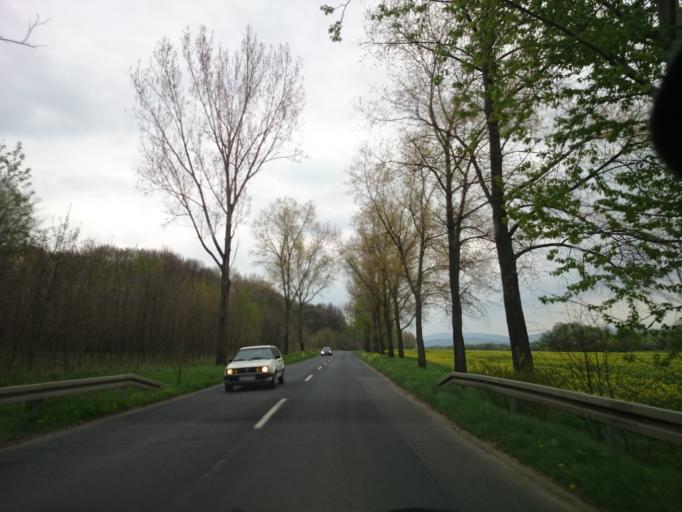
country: PL
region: Opole Voivodeship
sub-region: Powiat nyski
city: Nysa
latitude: 50.4042
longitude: 17.3418
